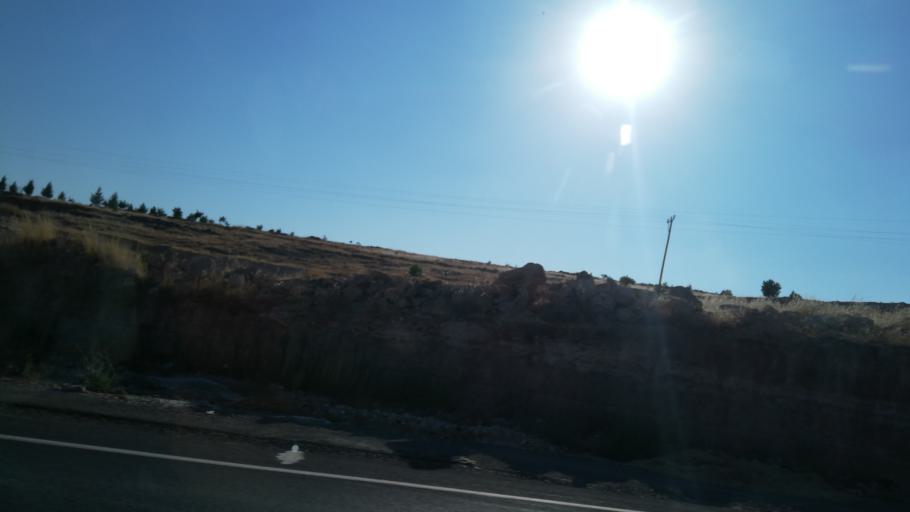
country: TR
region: Mardin
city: Midyat
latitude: 37.3981
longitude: 41.3446
